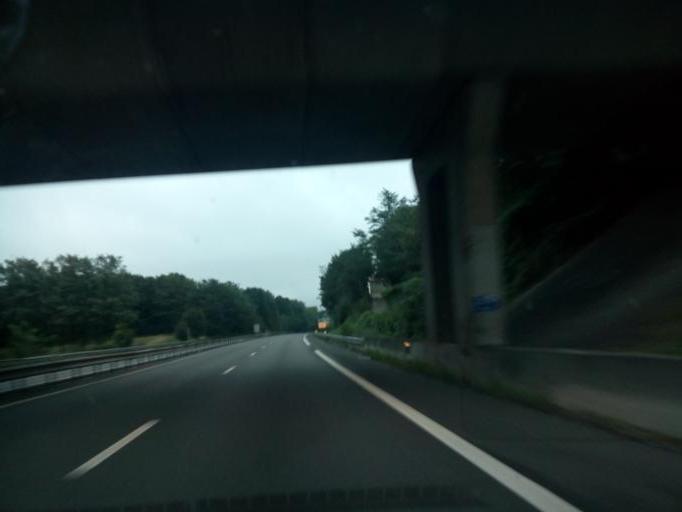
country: FR
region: Rhone-Alpes
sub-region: Departement de l'Isere
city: Aoste
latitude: 45.5769
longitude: 5.6124
